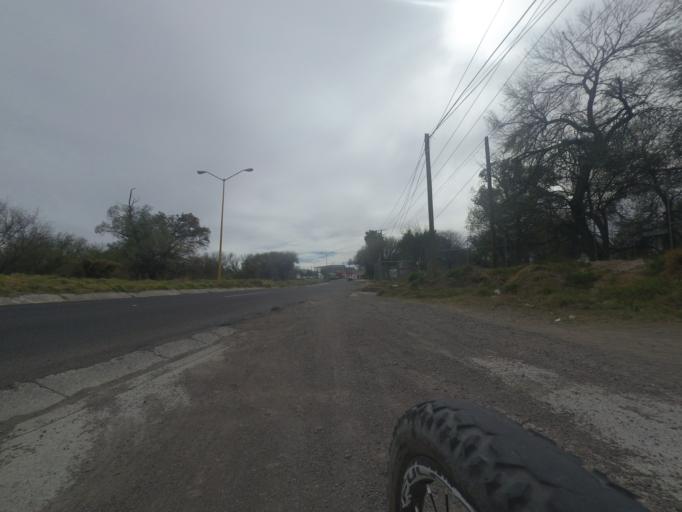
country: MX
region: Aguascalientes
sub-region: Aguascalientes
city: La Loma de los Negritos
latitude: 21.8453
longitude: -102.3540
